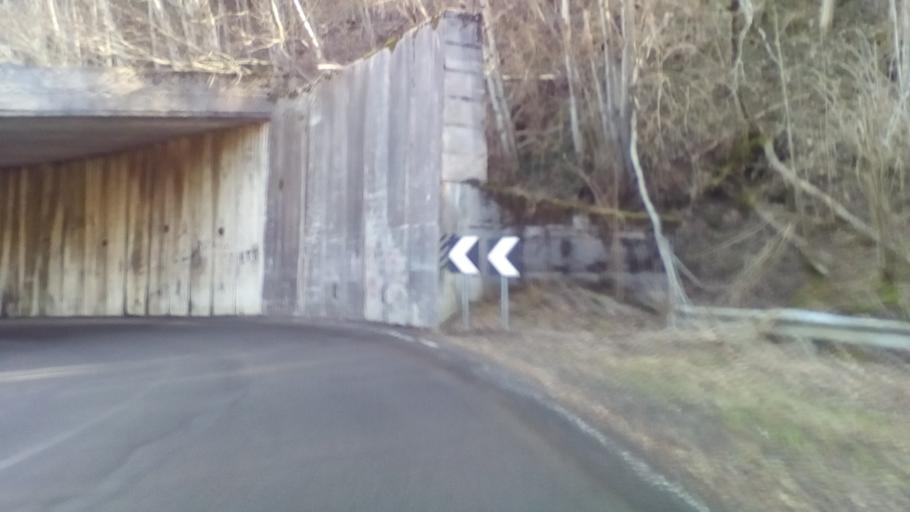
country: IT
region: Emilia-Romagna
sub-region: Provincia di Modena
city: Pievepelago
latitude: 44.1921
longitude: 10.5898
